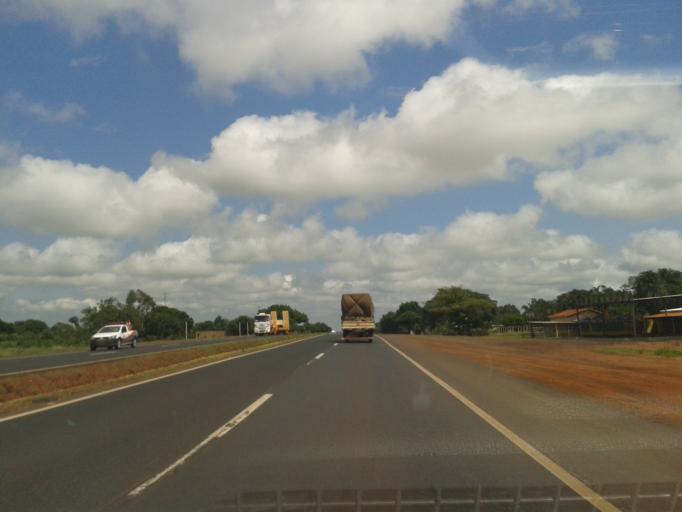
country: BR
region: Minas Gerais
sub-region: Centralina
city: Centralina
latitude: -18.7029
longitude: -49.1426
